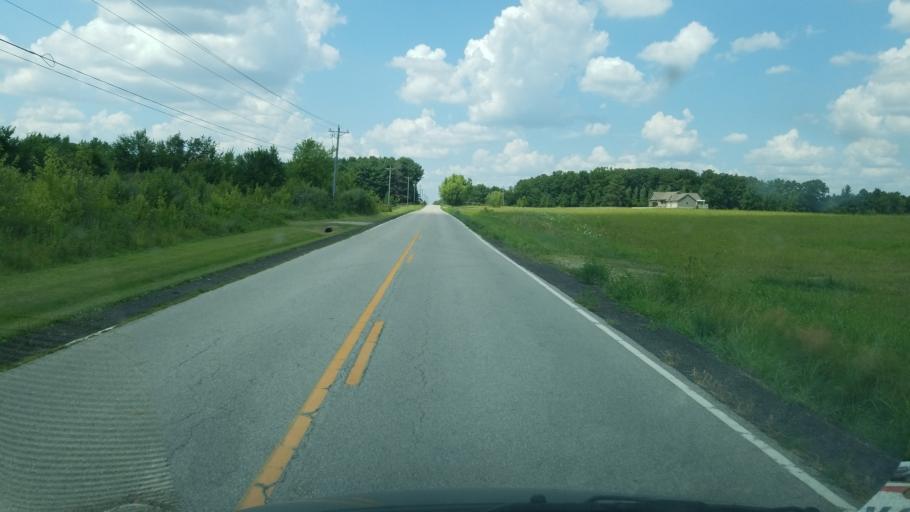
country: US
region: Ohio
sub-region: Champaign County
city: North Lewisburg
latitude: 40.2966
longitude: -83.4719
